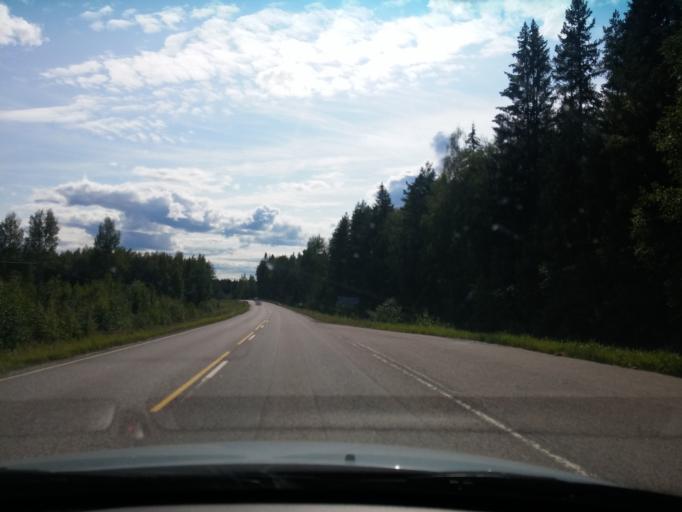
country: FI
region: Central Finland
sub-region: Keuruu
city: Keuruu
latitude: 62.2901
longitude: 24.7045
